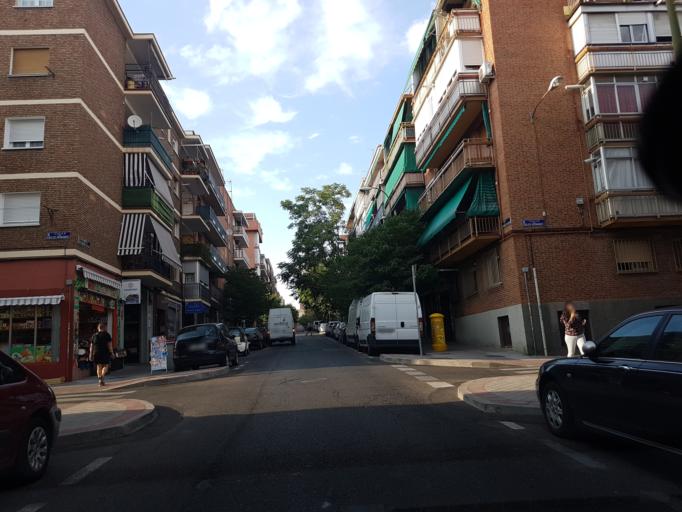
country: ES
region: Madrid
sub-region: Provincia de Madrid
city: Moratalaz
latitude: 40.4305
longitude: -3.6489
